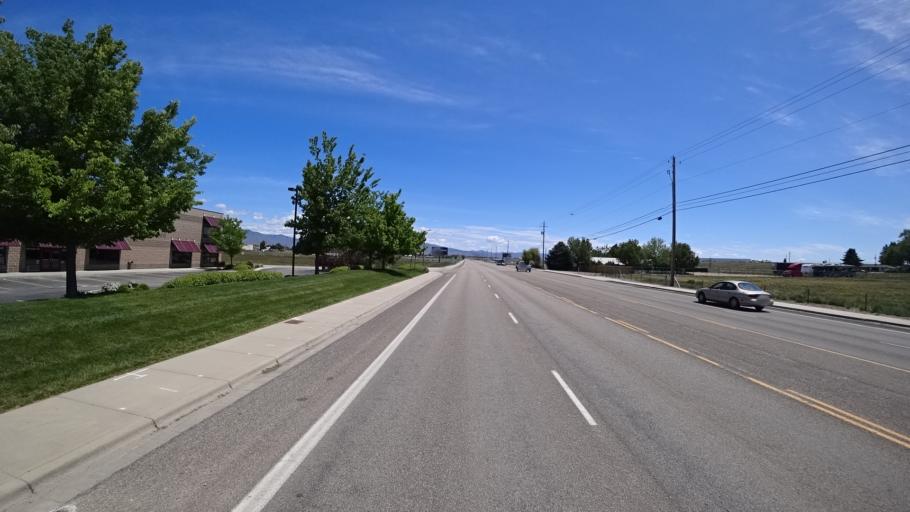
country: US
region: Idaho
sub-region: Ada County
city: Garden City
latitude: 43.5756
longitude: -116.2656
